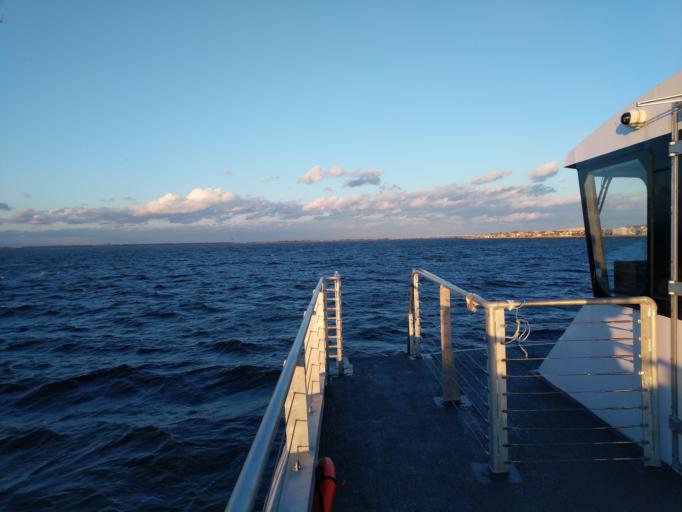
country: US
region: New York
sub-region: Kings County
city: East New York
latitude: 40.5775
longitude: -73.8676
